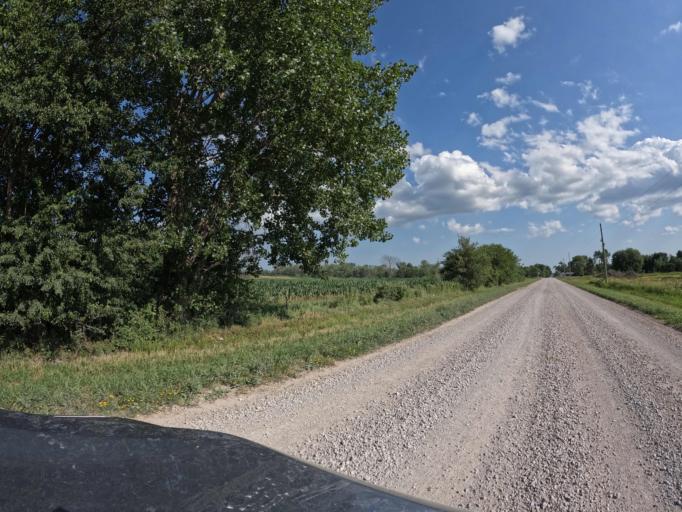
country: US
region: Iowa
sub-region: Appanoose County
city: Centerville
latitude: 40.7220
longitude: -93.0299
